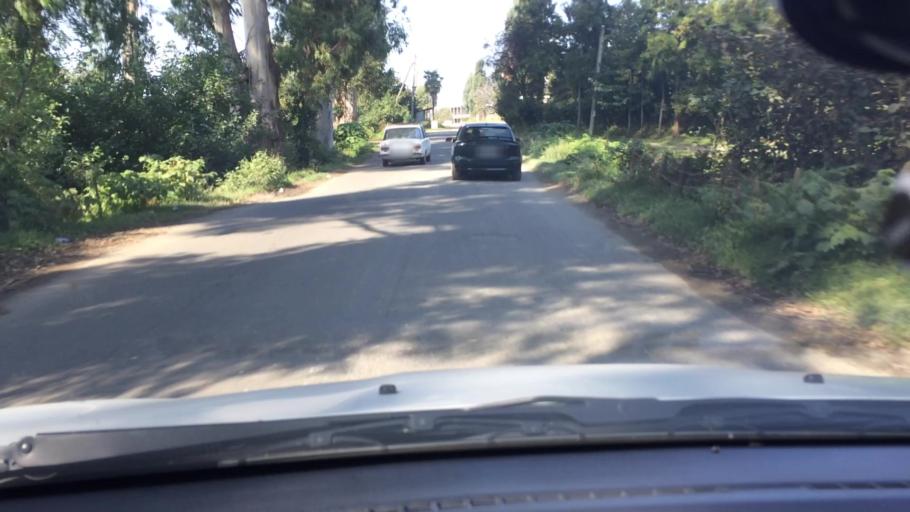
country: GE
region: Ajaria
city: Kobuleti
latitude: 41.8039
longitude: 41.8045
